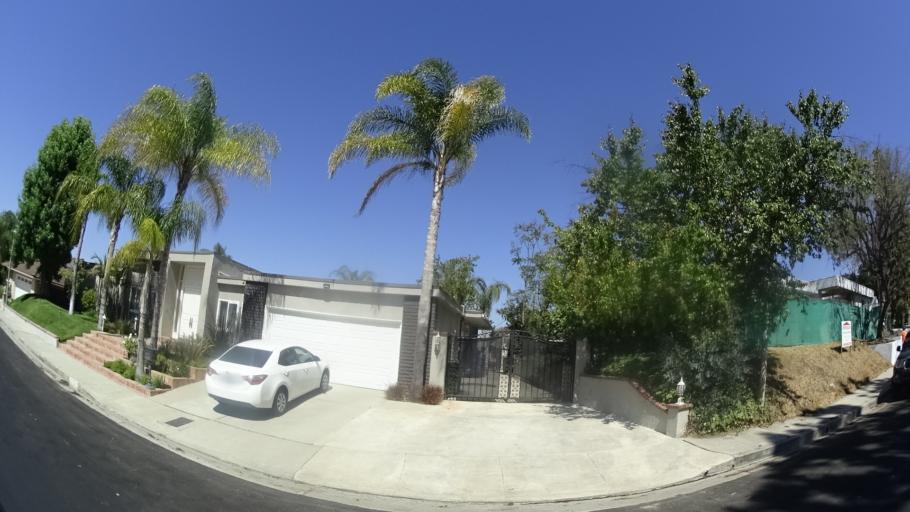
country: US
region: California
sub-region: Los Angeles County
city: Sherman Oaks
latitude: 34.1390
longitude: -118.4944
